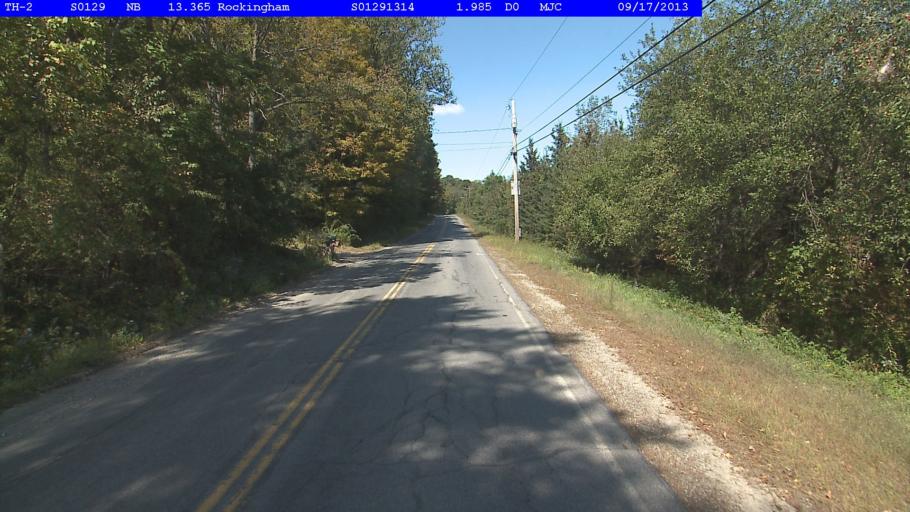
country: US
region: Vermont
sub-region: Windham County
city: Rockingham
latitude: 43.1461
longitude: -72.5185
